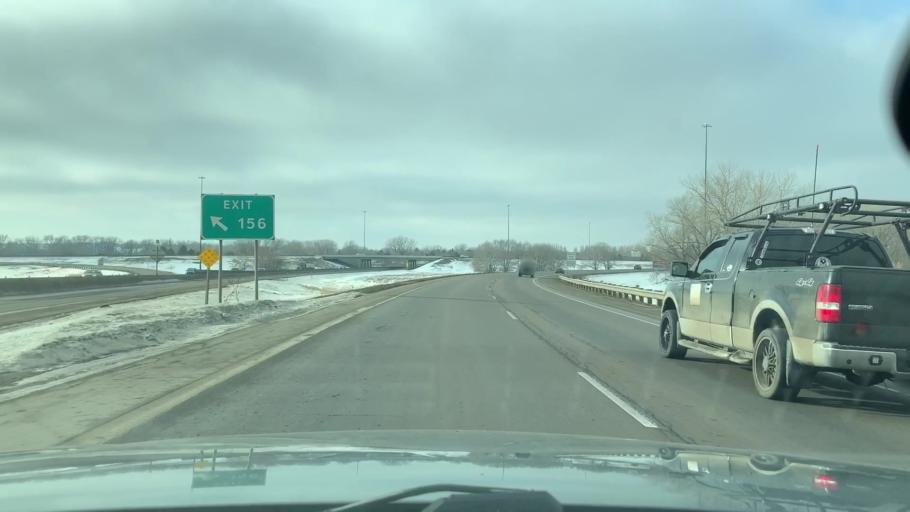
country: US
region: North Dakota
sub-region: Burleigh County
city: Bismarck
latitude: 46.8218
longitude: -100.8352
